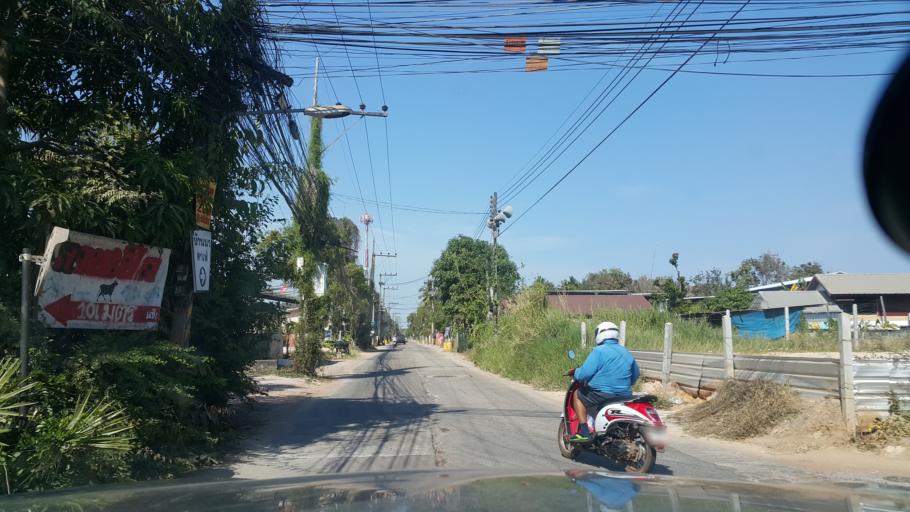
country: TH
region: Changwat Udon Thani
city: Udon Thani
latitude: 17.4561
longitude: 102.7793
